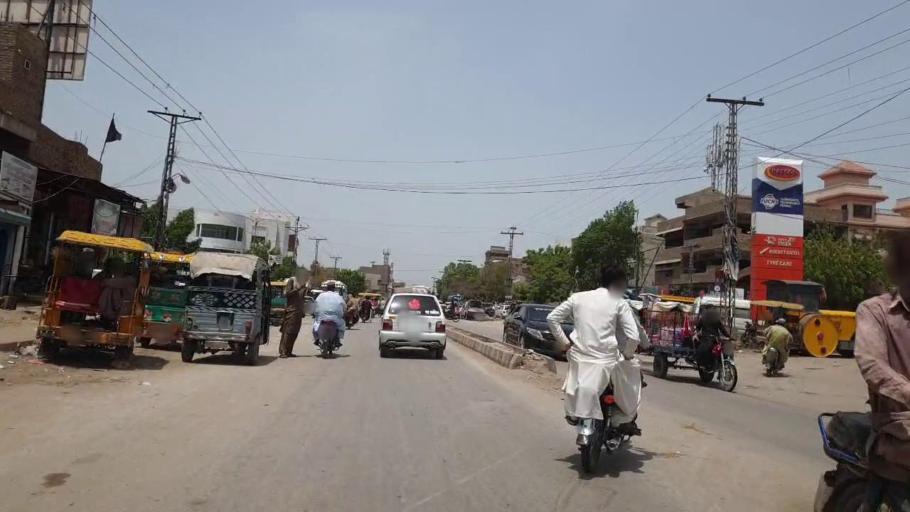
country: PK
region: Sindh
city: Nawabshah
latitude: 26.2517
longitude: 68.4146
